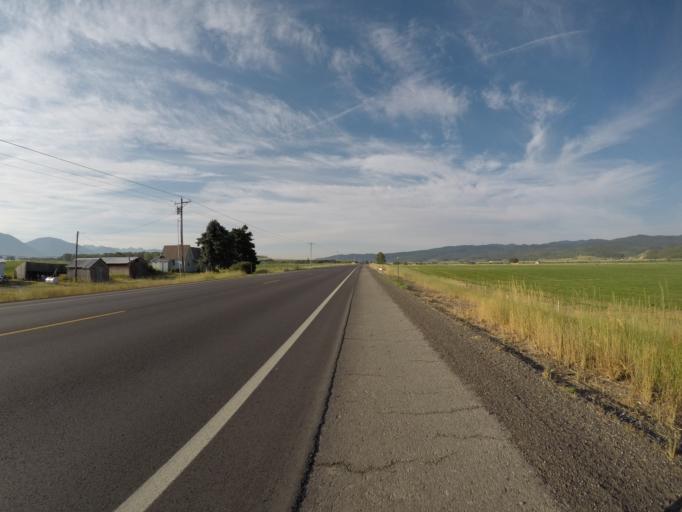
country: US
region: Wyoming
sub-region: Lincoln County
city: Afton
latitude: 42.9604
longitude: -111.0124
